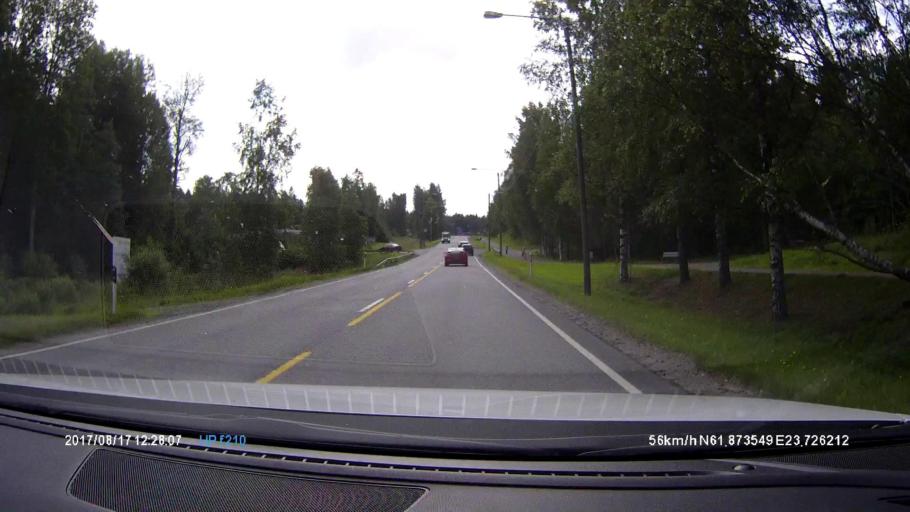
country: FI
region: Pirkanmaa
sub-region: Tampere
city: Kuru
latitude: 61.8733
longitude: 23.7263
